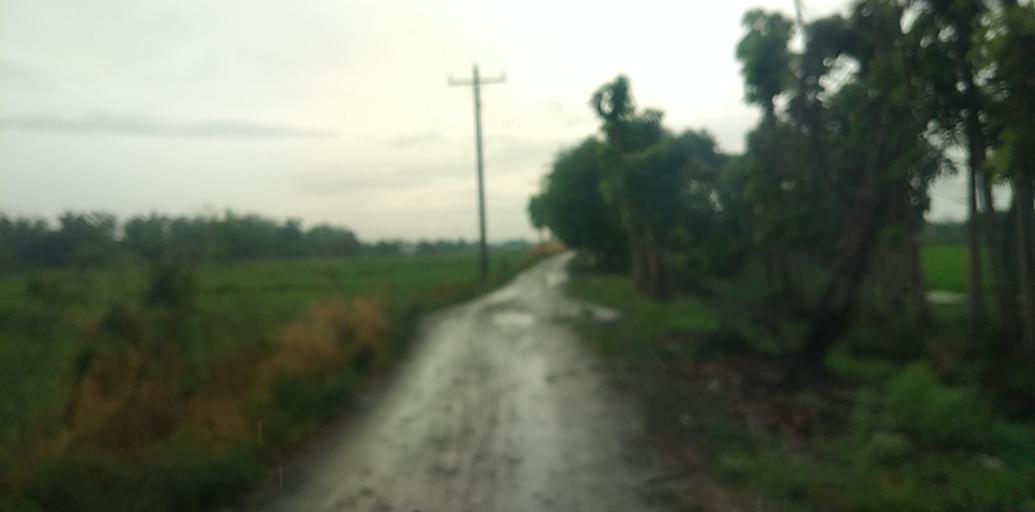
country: PH
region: Central Luzon
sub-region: Province of Pampanga
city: Panlinlang
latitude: 15.1590
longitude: 120.7180
